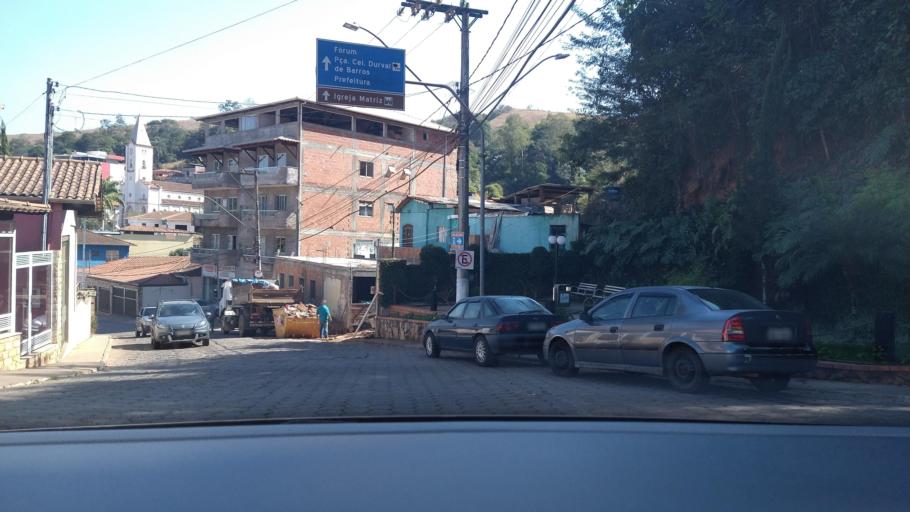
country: BR
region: Minas Gerais
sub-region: Rio Piracicaba
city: Rio Piracicaba
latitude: -19.9315
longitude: -43.1702
